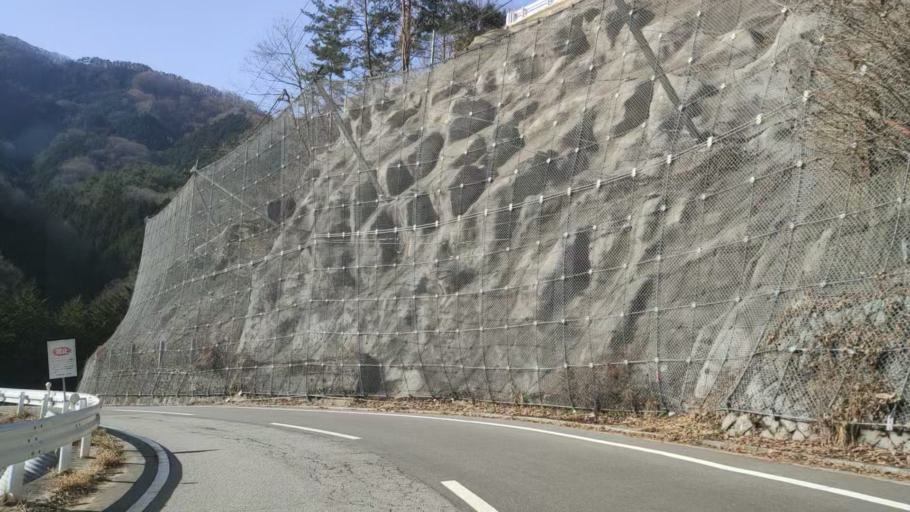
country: JP
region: Yamanashi
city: Fujikawaguchiko
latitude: 35.5509
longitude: 138.6558
